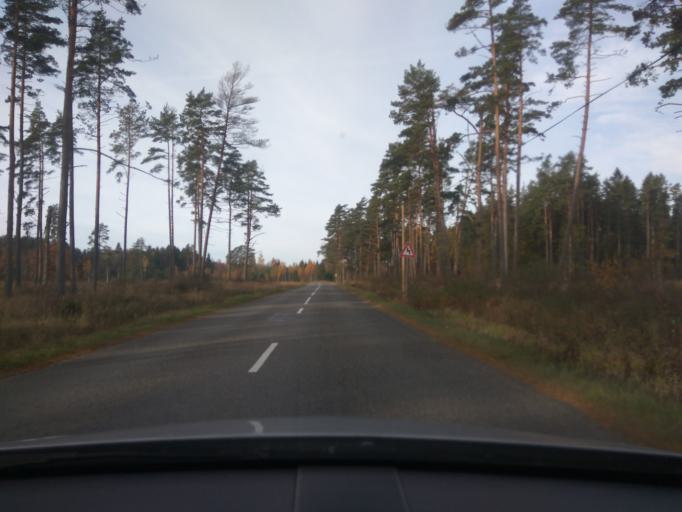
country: LV
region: Alsunga
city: Alsunga
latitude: 56.9880
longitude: 21.5175
